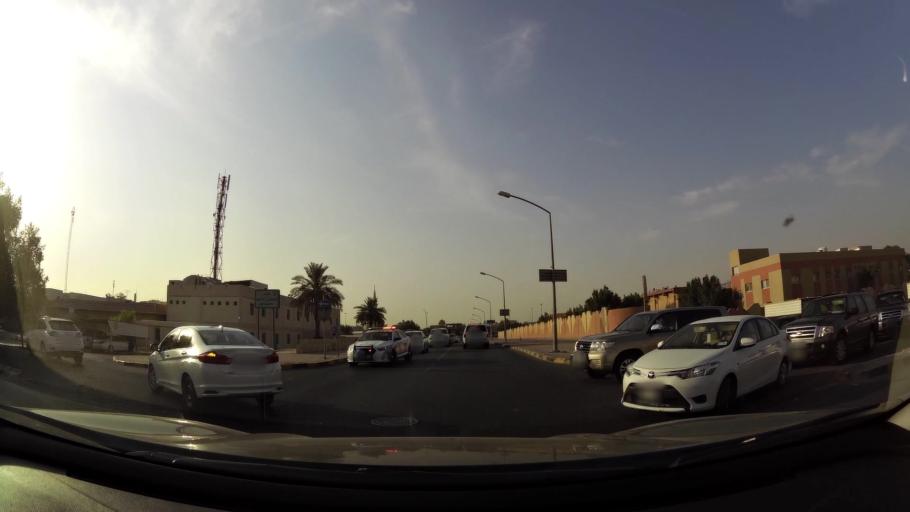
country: KW
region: Muhafazat Hawalli
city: Ar Rumaythiyah
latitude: 29.3185
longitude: 48.0767
